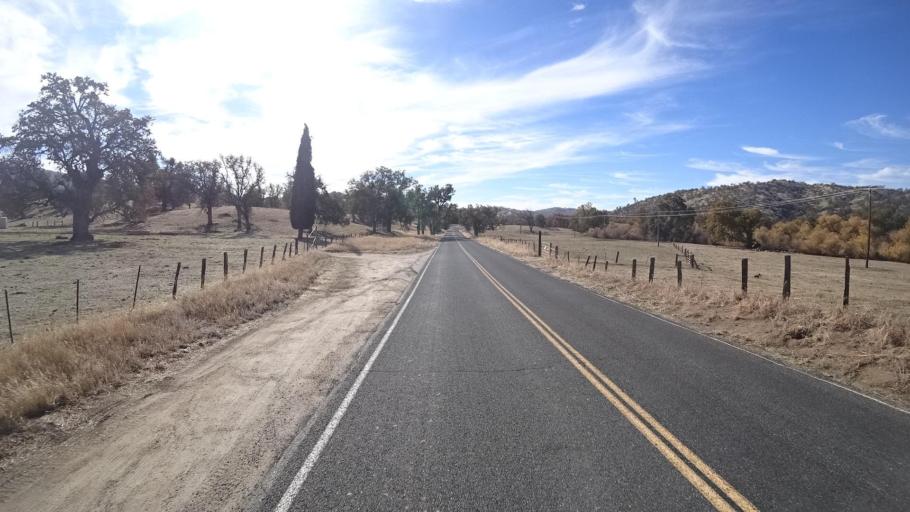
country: US
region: California
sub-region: Kern County
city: Alta Sierra
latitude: 35.6826
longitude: -118.7320
